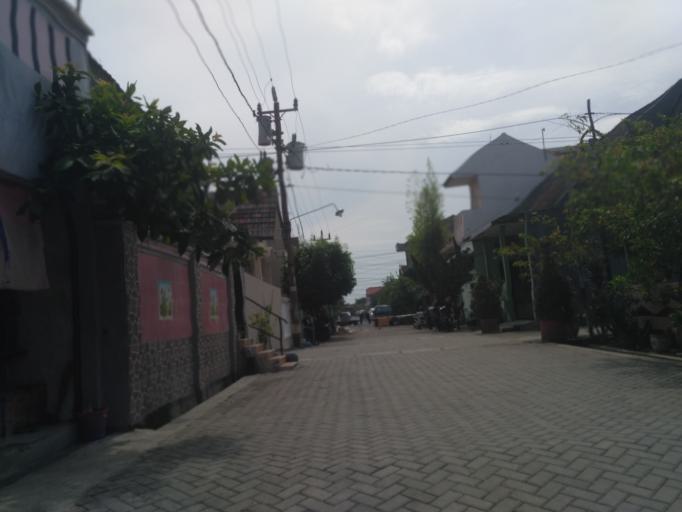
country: ID
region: Central Java
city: Semarang
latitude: -6.9578
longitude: 110.4029
